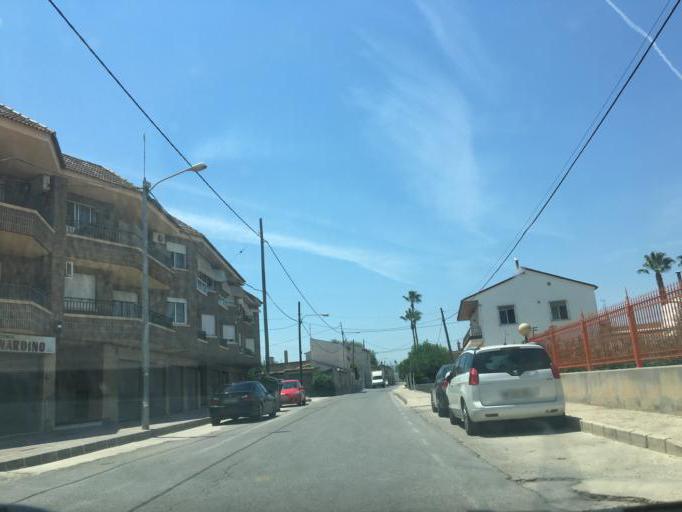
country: ES
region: Murcia
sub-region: Murcia
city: Santomera
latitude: 38.0304
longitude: -1.0638
